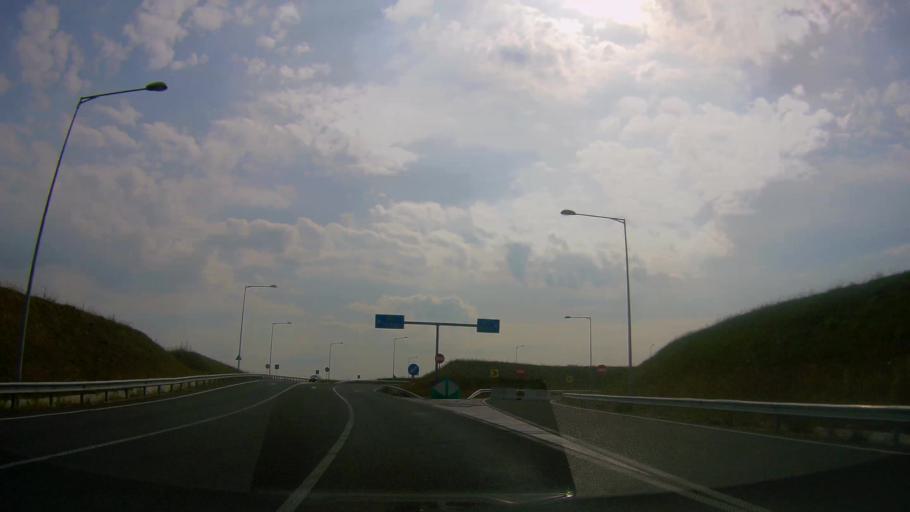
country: RO
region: Cluj
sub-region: Comuna Baciu
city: Mera
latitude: 46.8111
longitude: 23.4201
